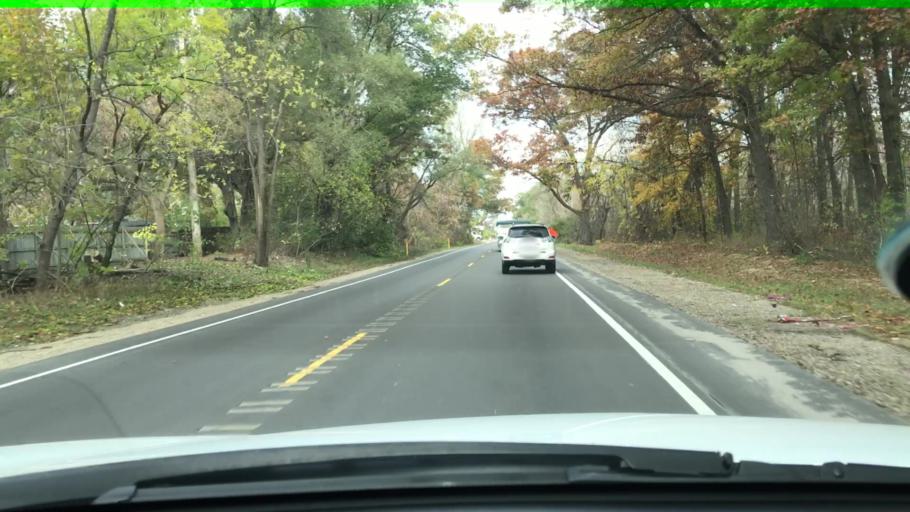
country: US
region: Michigan
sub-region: Oakland County
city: Waterford
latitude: 42.6494
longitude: -83.4435
